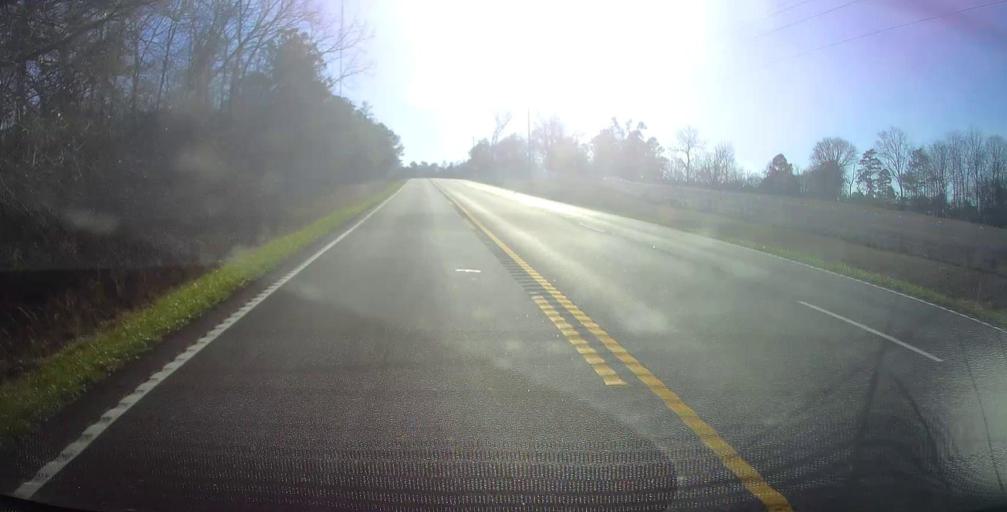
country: US
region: Georgia
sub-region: Meriwether County
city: Manchester
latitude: 32.8572
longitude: -84.6961
